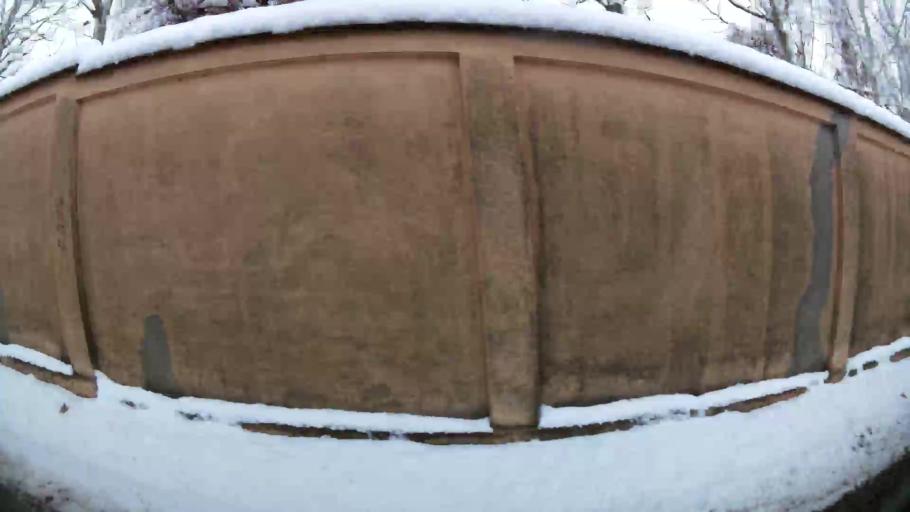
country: RO
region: Ilfov
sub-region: Comuna Tunari
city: Tunari
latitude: 44.5168
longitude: 26.1467
